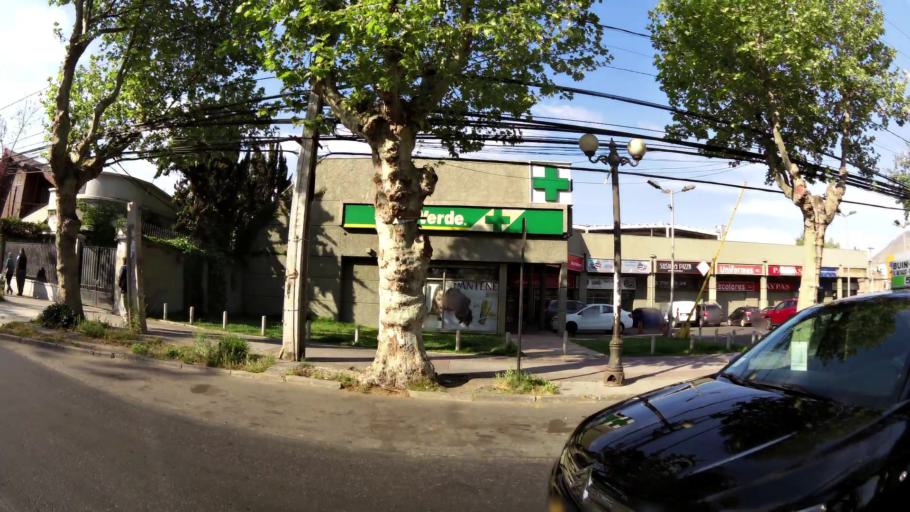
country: CL
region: Santiago Metropolitan
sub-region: Provincia de Maipo
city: San Bernardo
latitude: -33.5901
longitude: -70.7038
